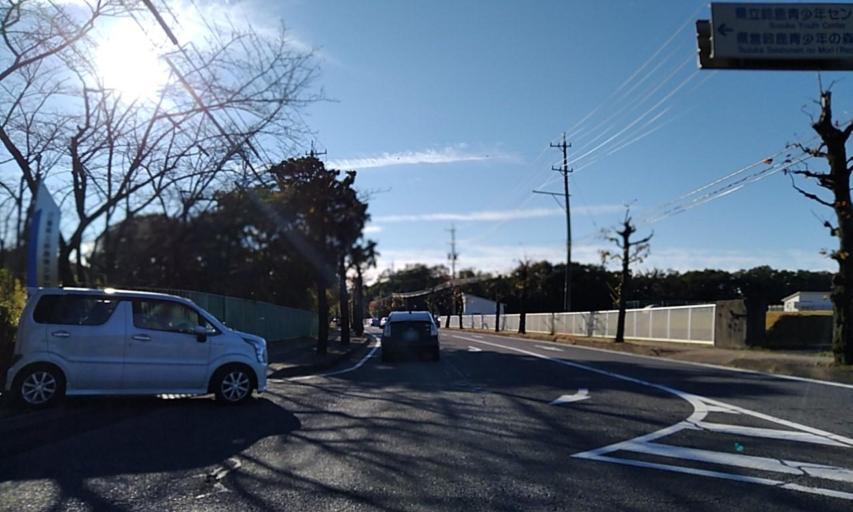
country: JP
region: Mie
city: Kawage
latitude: 34.8521
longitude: 136.5342
